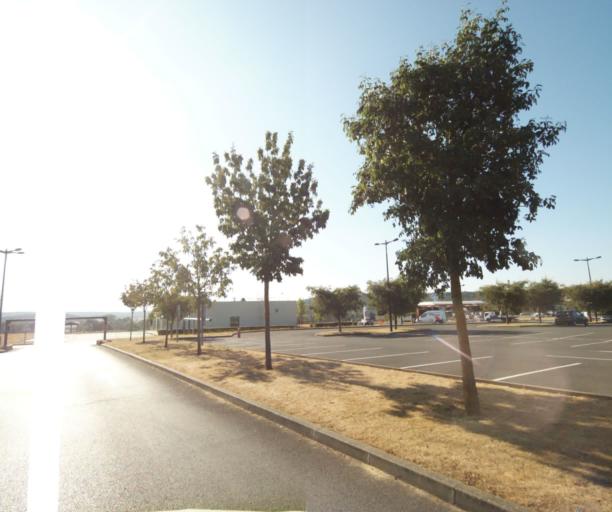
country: FR
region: Ile-de-France
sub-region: Departement de l'Essonne
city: Baulne
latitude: 48.5007
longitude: 2.3507
